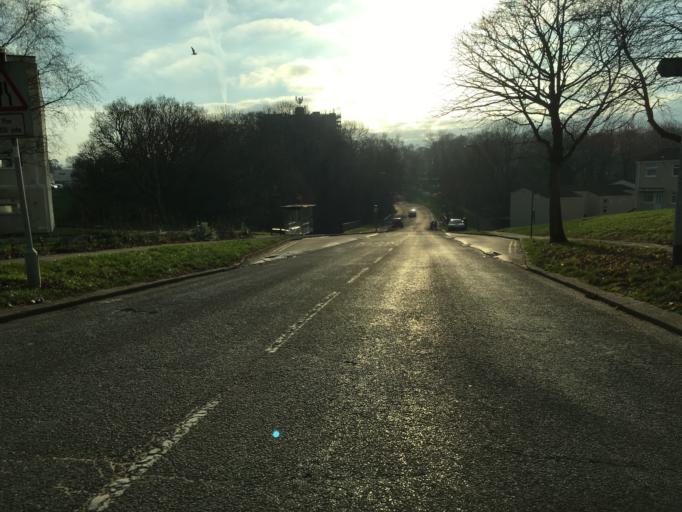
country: GB
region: Wales
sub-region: Cardiff
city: Cardiff
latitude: 51.5158
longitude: -3.1519
